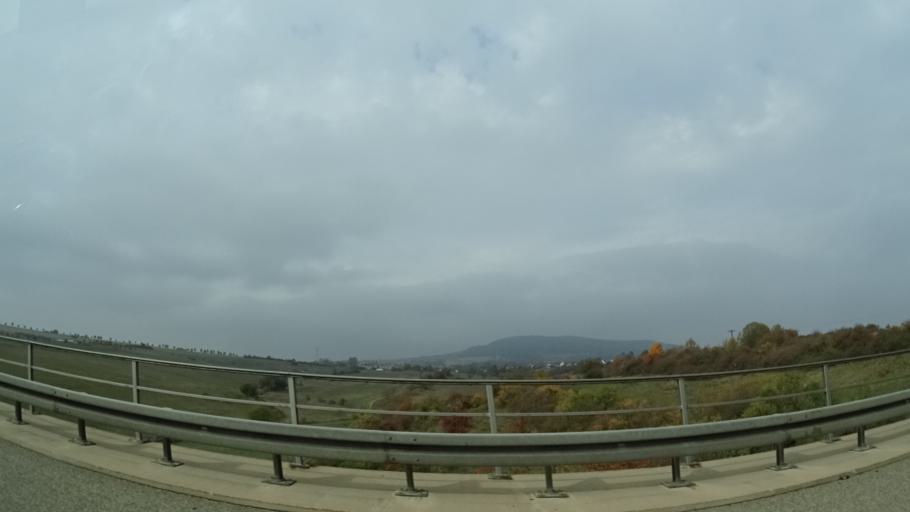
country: DE
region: Thuringia
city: Rohr
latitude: 50.5968
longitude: 10.4987
